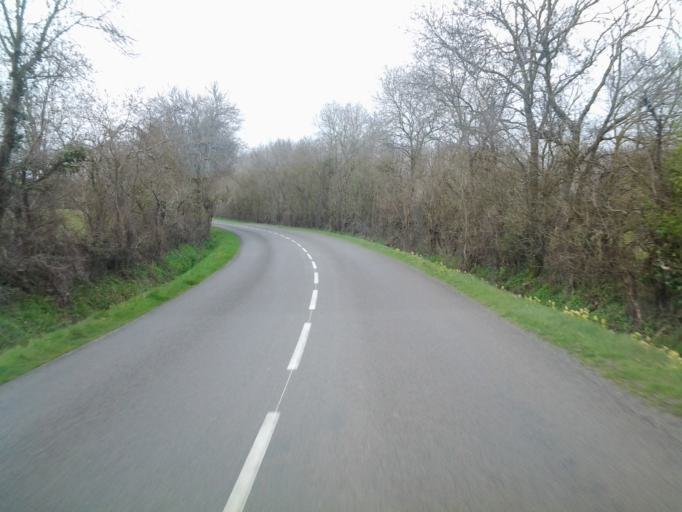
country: FR
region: Pays de la Loire
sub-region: Departement de la Vendee
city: Avrille
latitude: 46.4447
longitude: -1.4843
